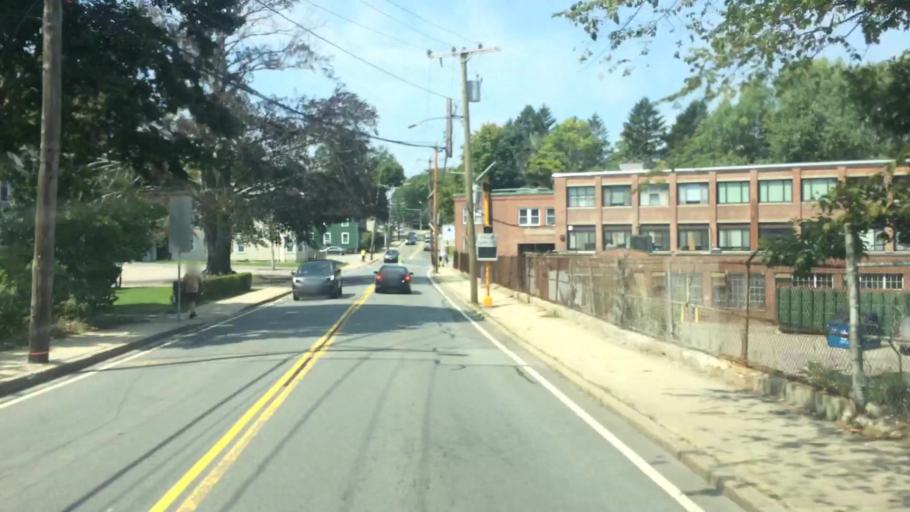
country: US
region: Massachusetts
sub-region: Norfolk County
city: Dedham
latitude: 42.2480
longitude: -71.1593
